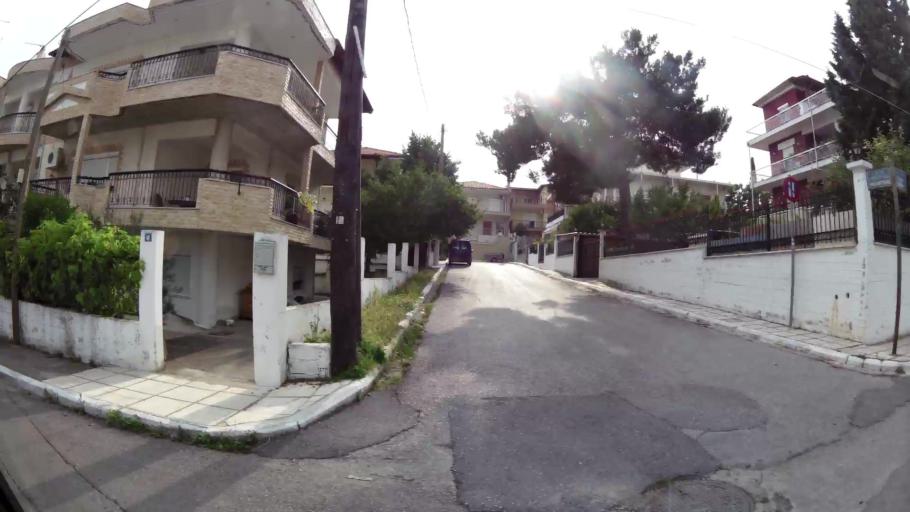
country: GR
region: Central Macedonia
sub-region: Nomos Thessalonikis
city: Oraiokastro
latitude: 40.7297
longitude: 22.9204
